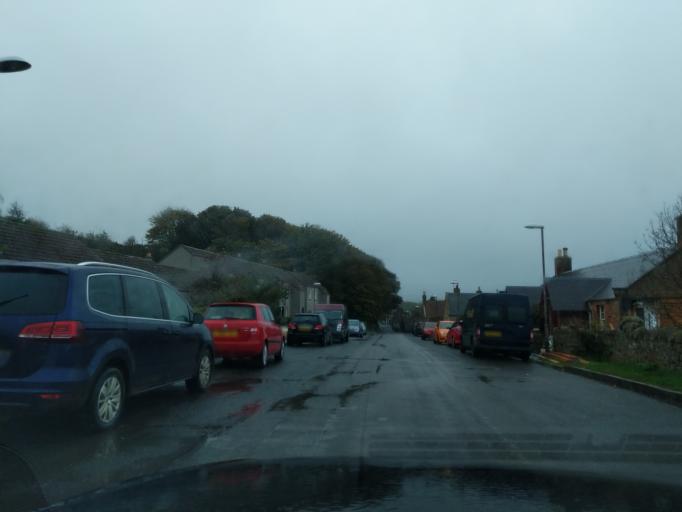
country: GB
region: Scotland
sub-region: East Lothian
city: Dunbar
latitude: 55.9570
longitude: -2.4436
